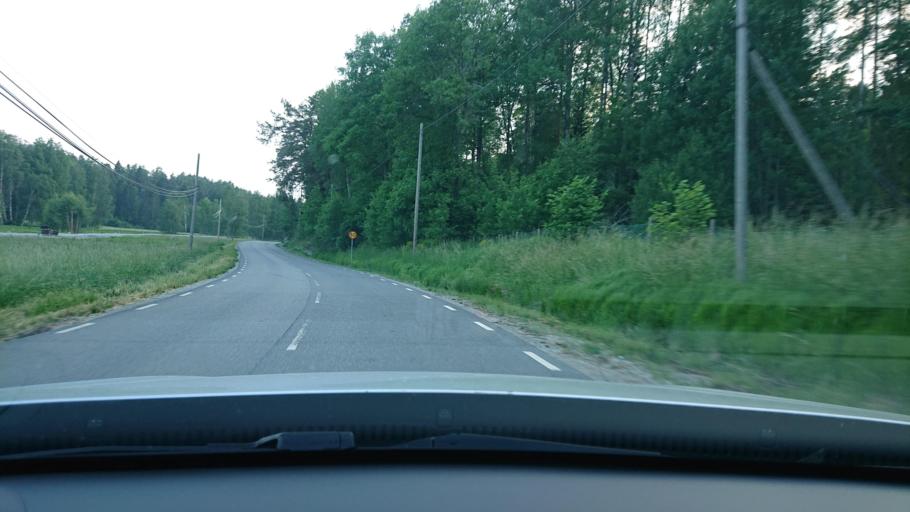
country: SE
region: Stockholm
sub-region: Vaxholms Kommun
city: Resaro
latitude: 59.4701
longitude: 18.3674
